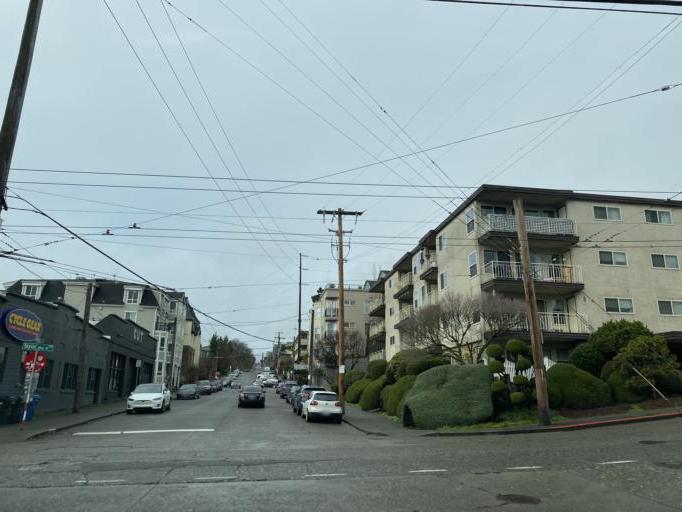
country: US
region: Washington
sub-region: King County
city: Seattle
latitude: 47.6272
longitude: -122.3461
